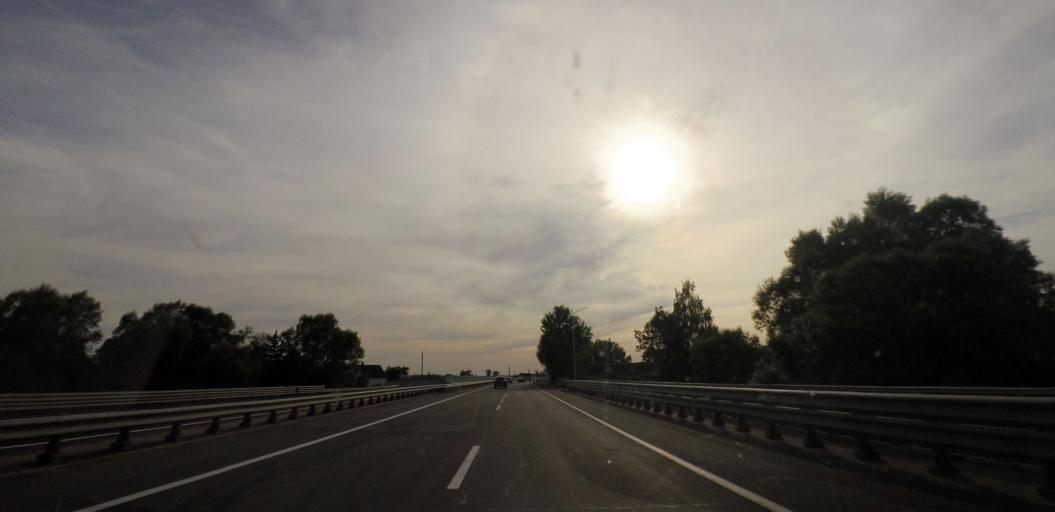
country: BY
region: Grodnenskaya
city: Skidal'
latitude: 53.5788
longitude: 24.2606
